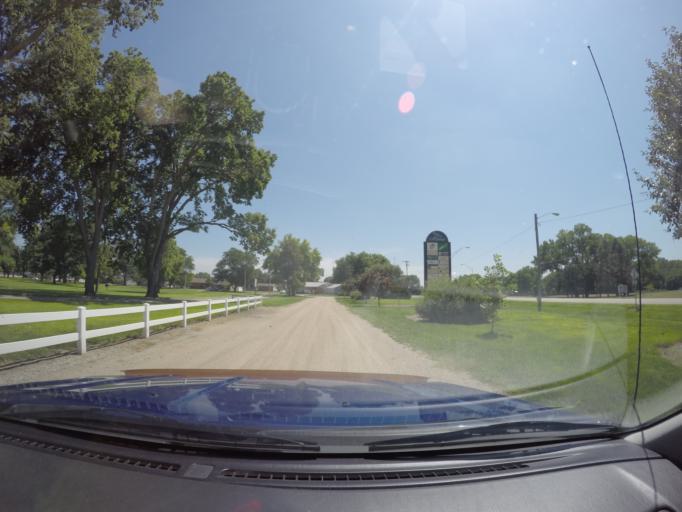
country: US
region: Nebraska
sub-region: Harlan County
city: Alma
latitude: 40.0987
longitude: -99.3700
